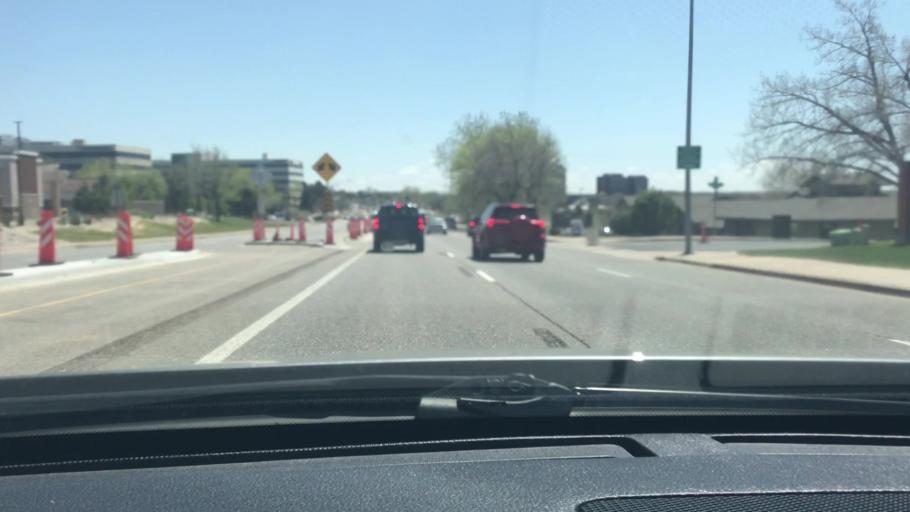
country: US
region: Colorado
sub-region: Adams County
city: Aurora
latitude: 39.6728
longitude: -104.8685
